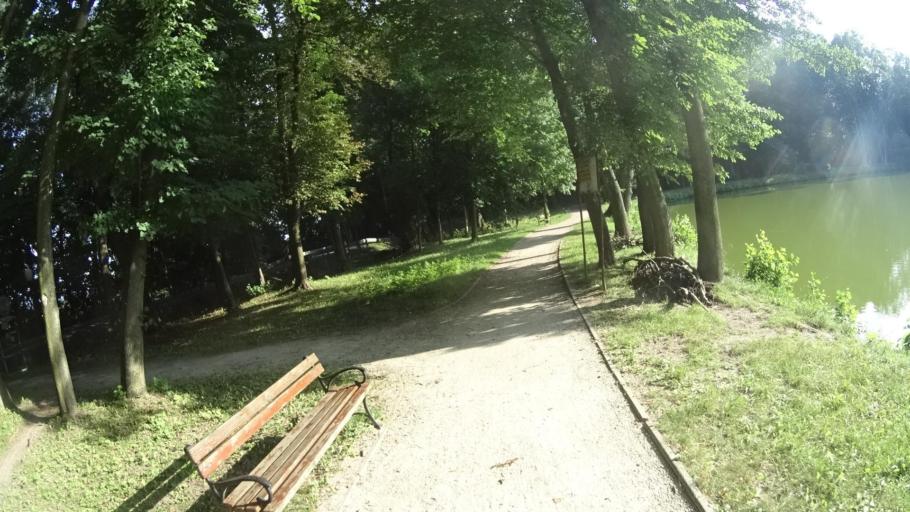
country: PL
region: Masovian Voivodeship
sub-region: Powiat pruszkowski
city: Nadarzyn
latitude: 52.0445
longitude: 20.7832
